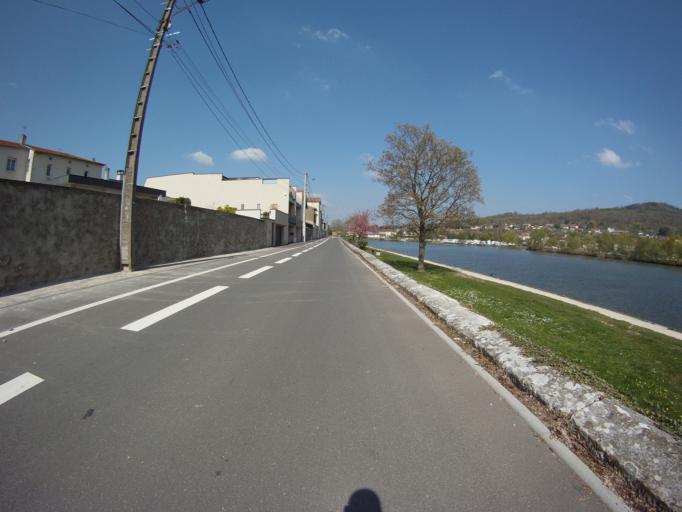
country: FR
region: Lorraine
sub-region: Departement de Meurthe-et-Moselle
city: Pont-a-Mousson
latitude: 48.9005
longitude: 6.0591
